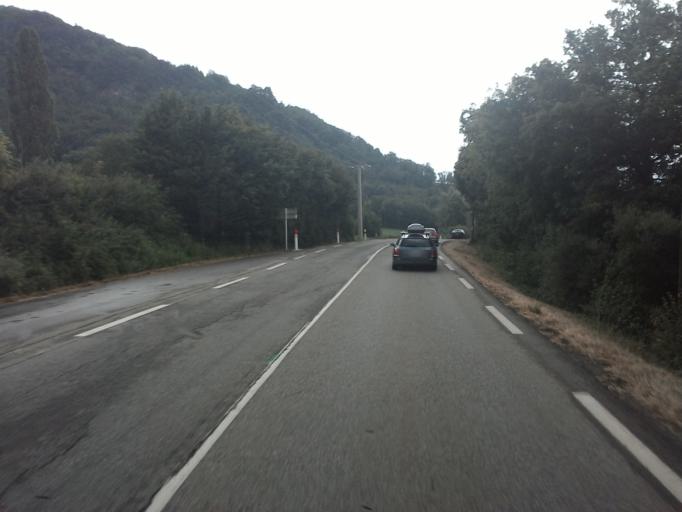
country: FR
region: Provence-Alpes-Cote d'Azur
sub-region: Departement des Hautes-Alpes
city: Saint-Bonnet-en-Champsaur
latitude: 44.7906
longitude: 5.9809
